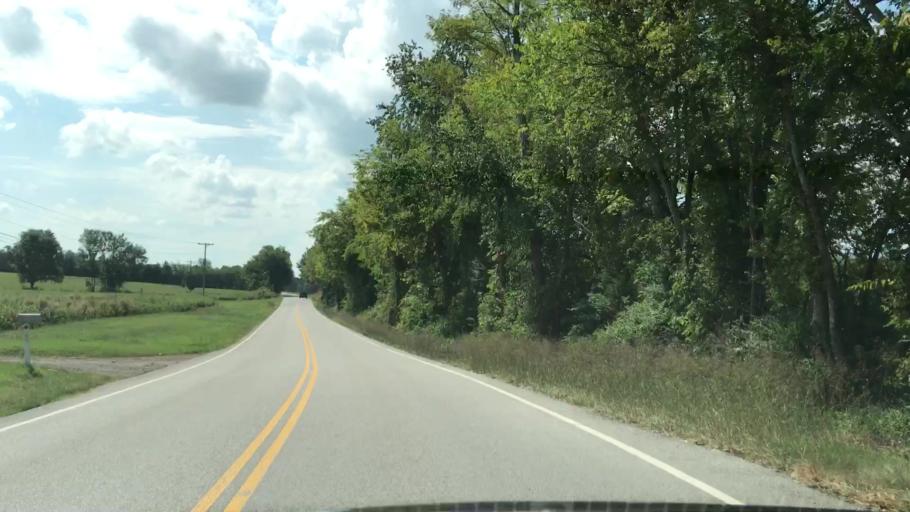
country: US
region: Tennessee
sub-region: Trousdale County
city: Hartsville
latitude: 36.4170
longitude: -86.1807
